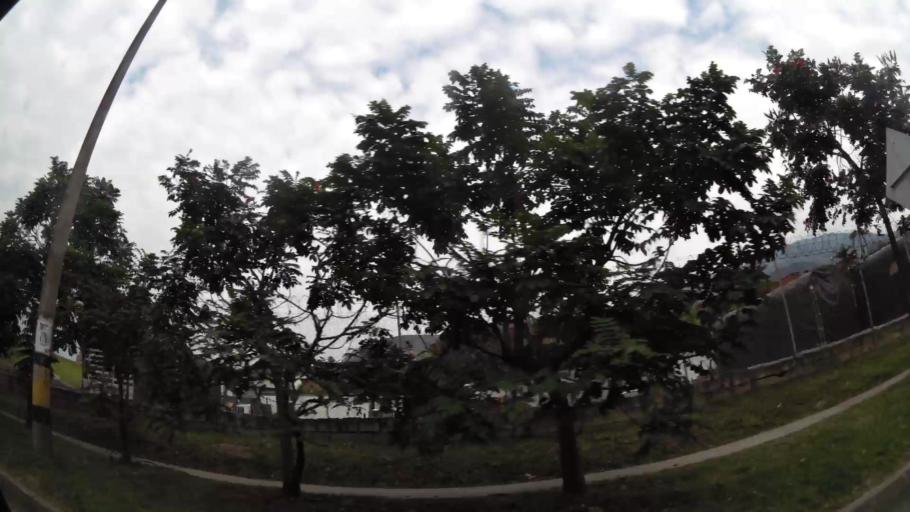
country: CO
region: Antioquia
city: Bello
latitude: 6.3079
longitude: -75.5566
